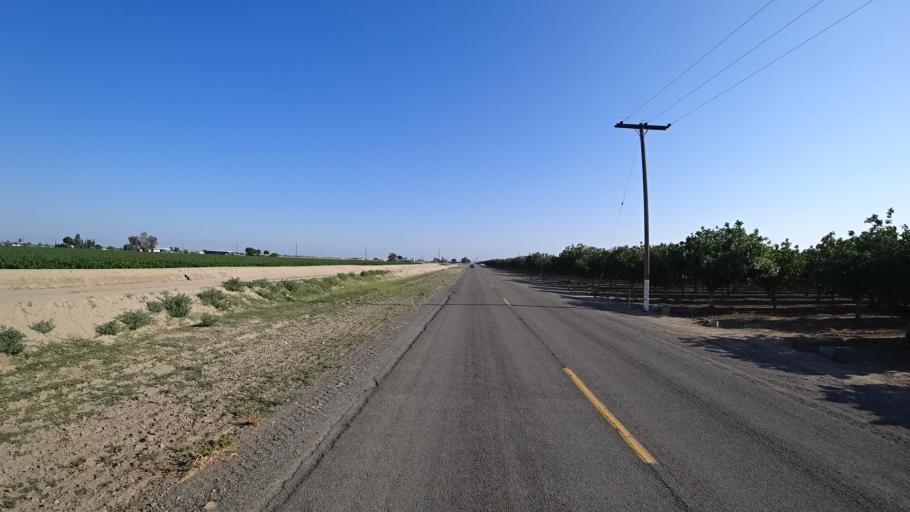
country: US
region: California
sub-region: Kings County
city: Home Garden
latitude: 36.3102
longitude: -119.5652
